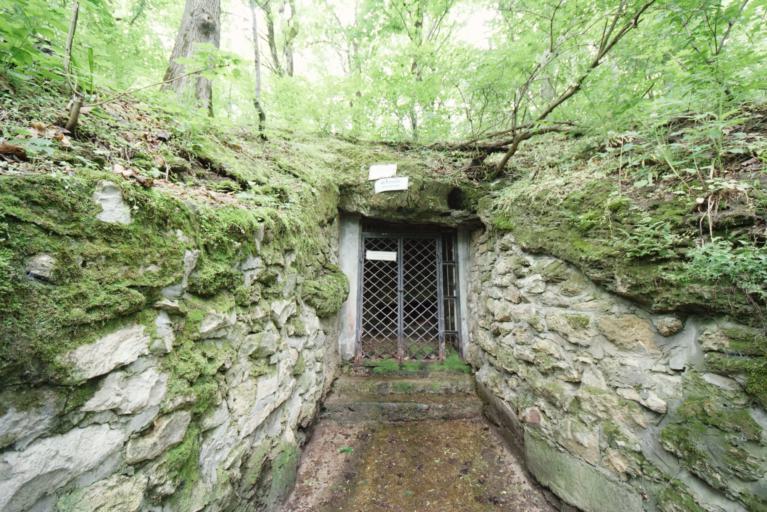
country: RU
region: Stavropol'skiy
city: Zheleznovodsk
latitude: 44.1382
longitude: 43.0385
